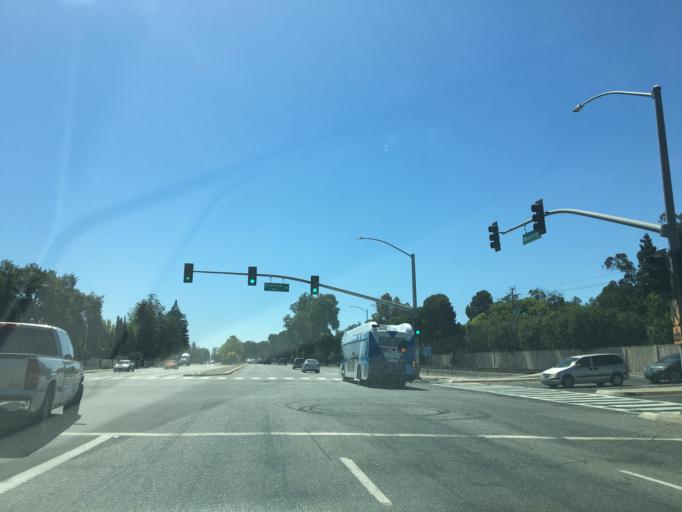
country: US
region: California
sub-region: Santa Clara County
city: Seven Trees
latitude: 37.2677
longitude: -121.8225
